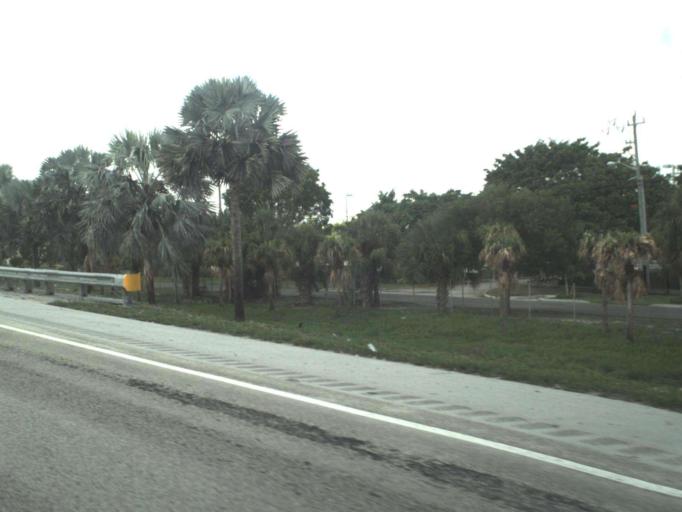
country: US
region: Florida
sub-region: Broward County
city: Kendall Green
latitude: 26.2473
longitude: -80.1368
